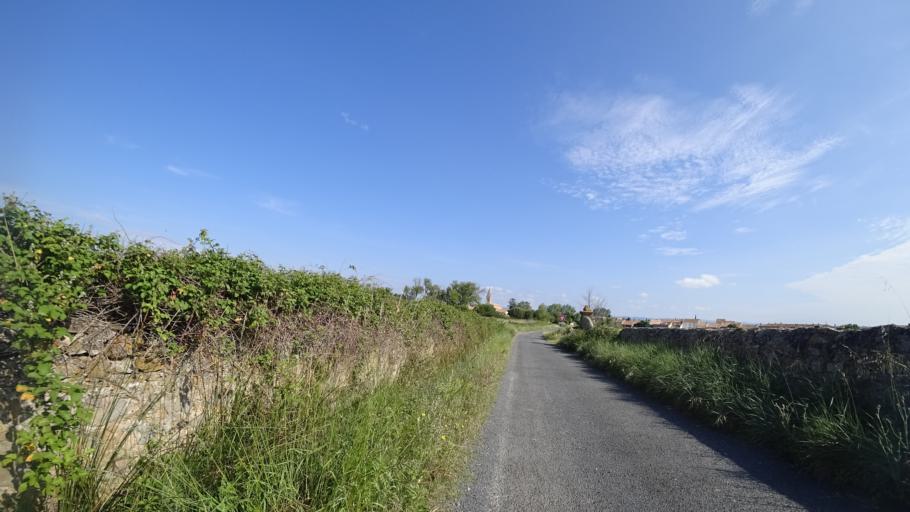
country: FR
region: Languedoc-Roussillon
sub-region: Departement de l'Herault
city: Olonzac
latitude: 43.2641
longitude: 2.7211
